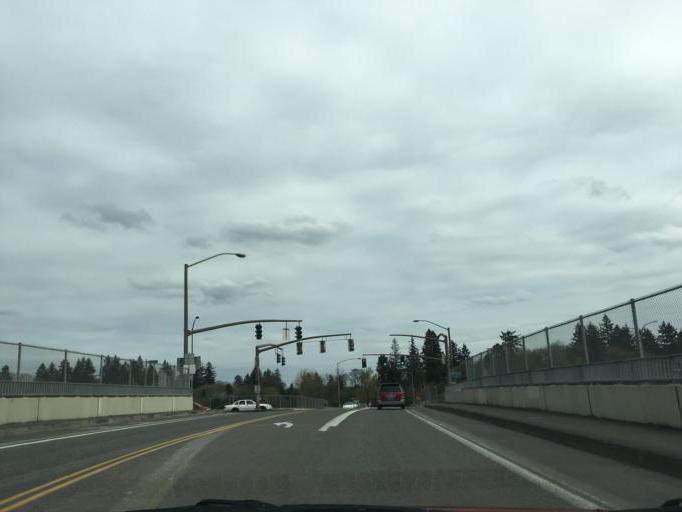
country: US
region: Oregon
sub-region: Clackamas County
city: Milwaukie
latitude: 45.4643
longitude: -122.6384
